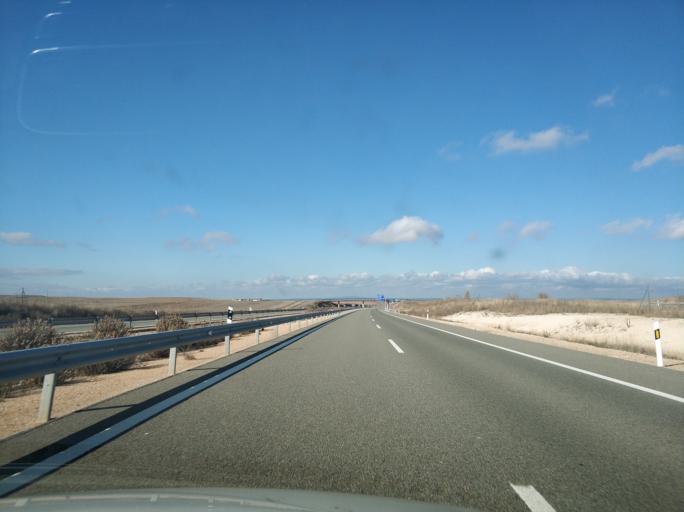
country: ES
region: Castille and Leon
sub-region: Provincia de Soria
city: Coscurita
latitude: 41.4078
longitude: -2.4821
